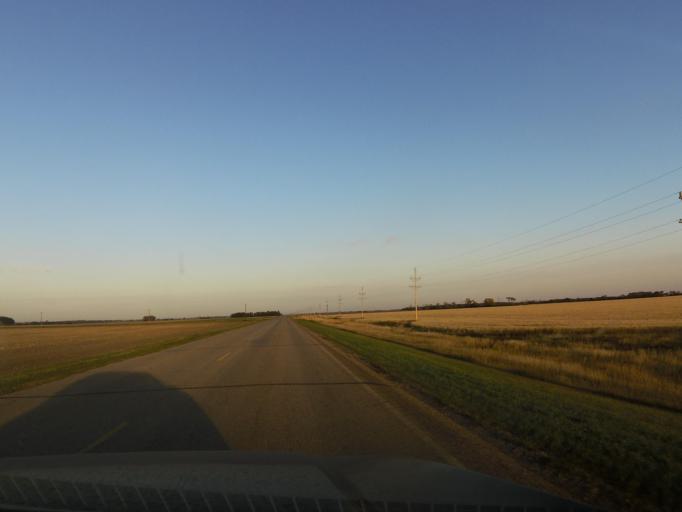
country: CA
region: Manitoba
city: Altona
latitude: 48.9632
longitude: -97.6114
